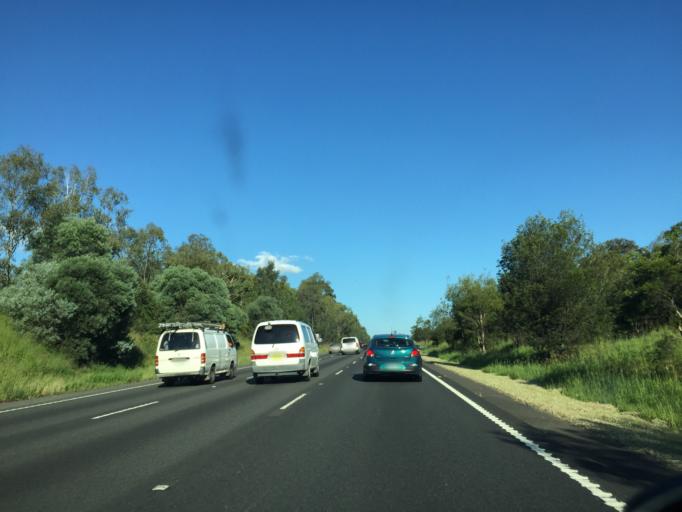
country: AU
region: New South Wales
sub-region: Blacktown
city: Mount Druitt
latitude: -33.7880
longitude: 150.7915
